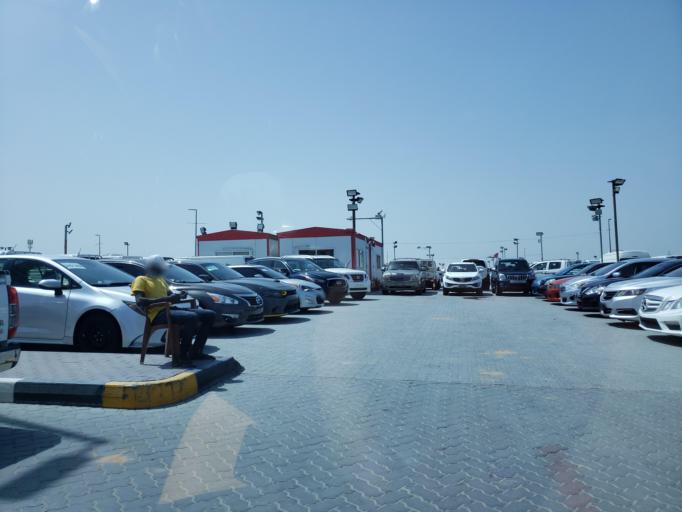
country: AE
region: Ash Shariqah
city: Sharjah
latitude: 25.3410
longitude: 55.4777
